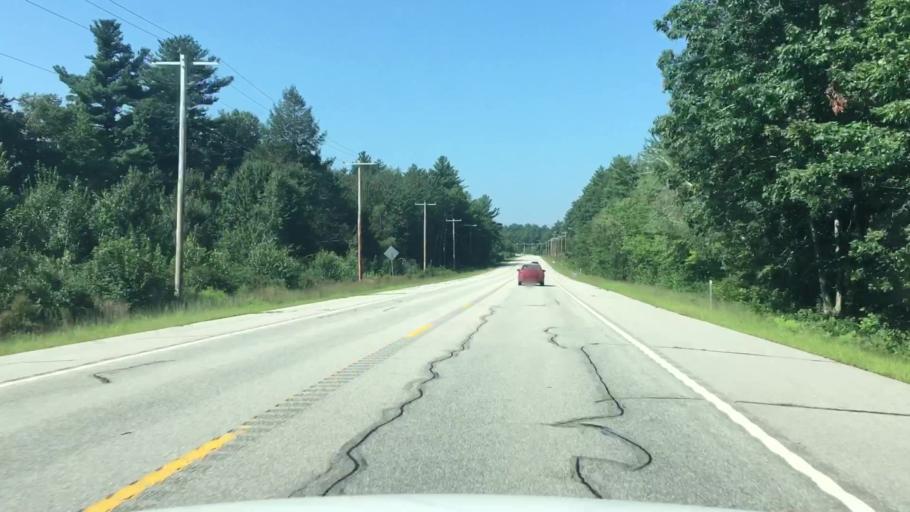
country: US
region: New Hampshire
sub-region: Rockingham County
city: Danville
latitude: 42.9079
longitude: -71.0906
